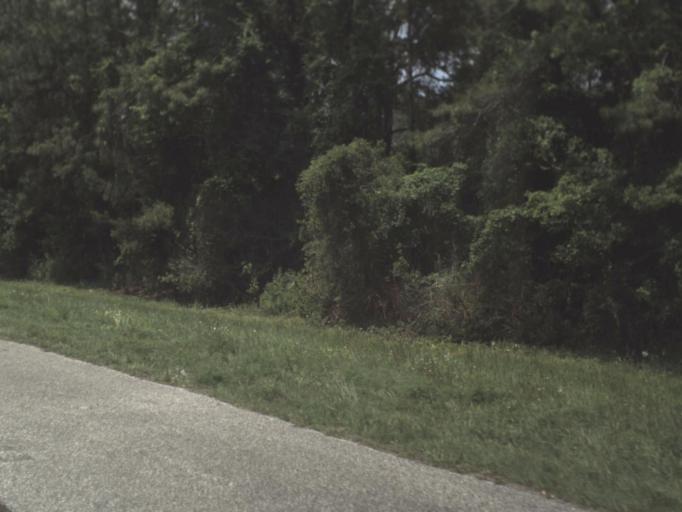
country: US
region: Florida
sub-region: Saint Johns County
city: Fruit Cove
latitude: 30.1756
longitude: -81.6193
